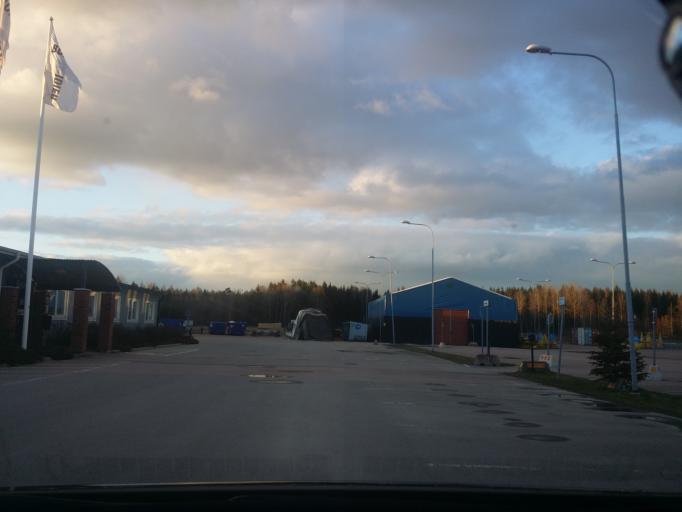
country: SE
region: Vaestmanland
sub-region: Vasteras
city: Hokasen
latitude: 59.6510
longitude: 16.5911
